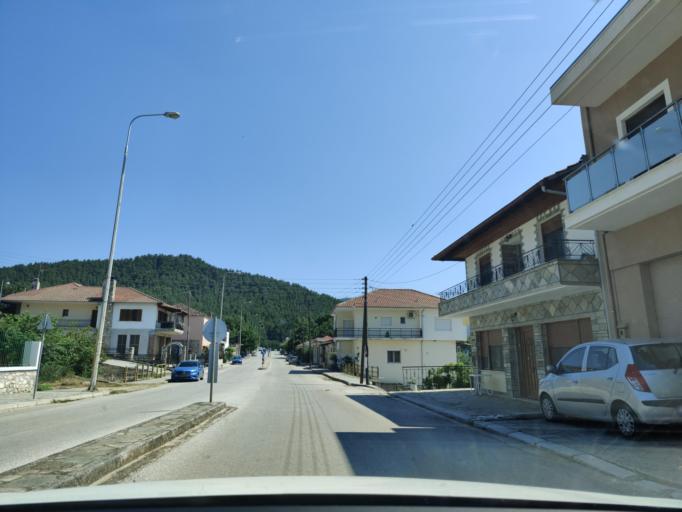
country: GR
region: East Macedonia and Thrace
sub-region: Nomos Kavalas
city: Zygos
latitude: 41.0123
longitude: 24.3817
